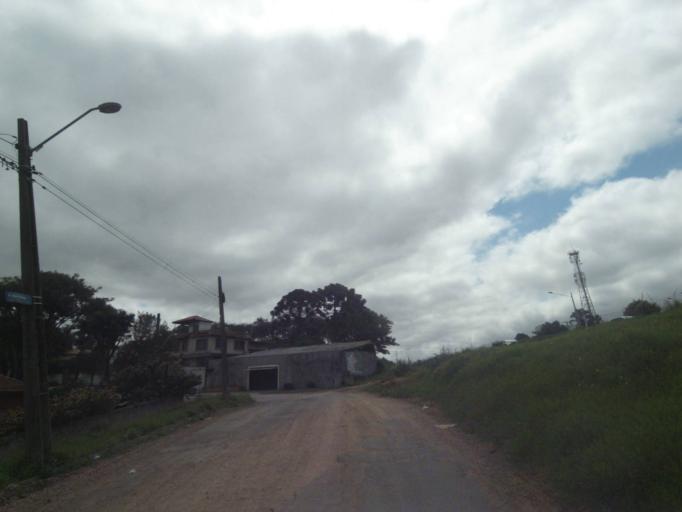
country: BR
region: Parana
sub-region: Pinhais
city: Pinhais
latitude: -25.3951
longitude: -49.2122
